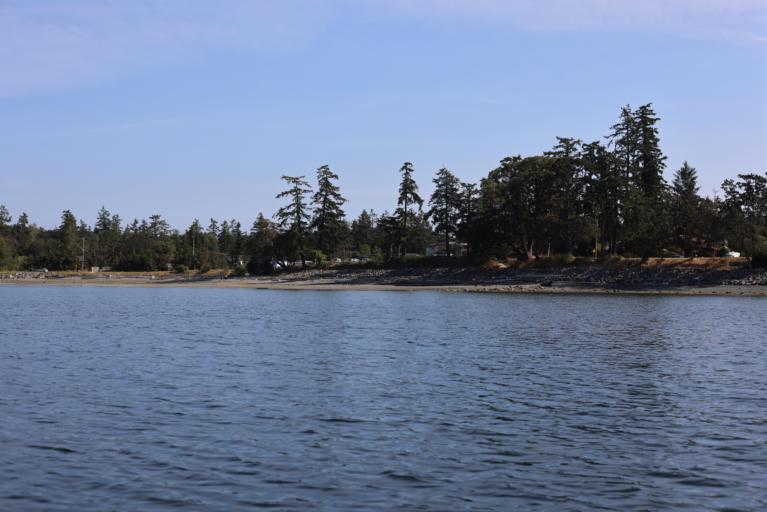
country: CA
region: British Columbia
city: North Saanich
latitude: 48.6598
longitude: -123.4518
